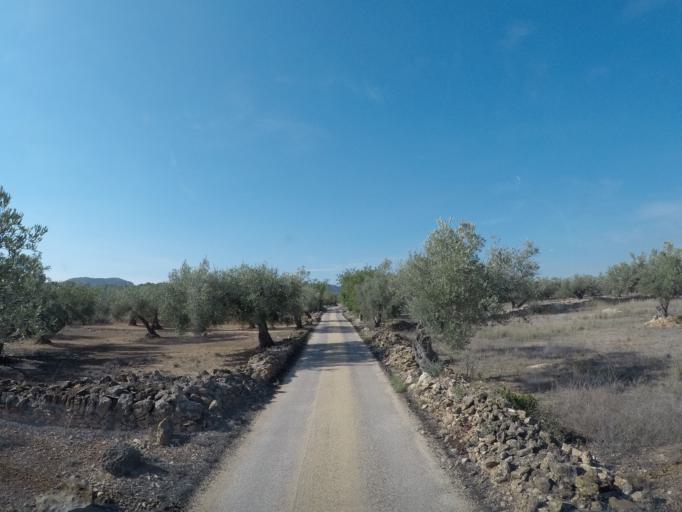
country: ES
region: Catalonia
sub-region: Provincia de Tarragona
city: El Perello
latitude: 40.8996
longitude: 0.7317
